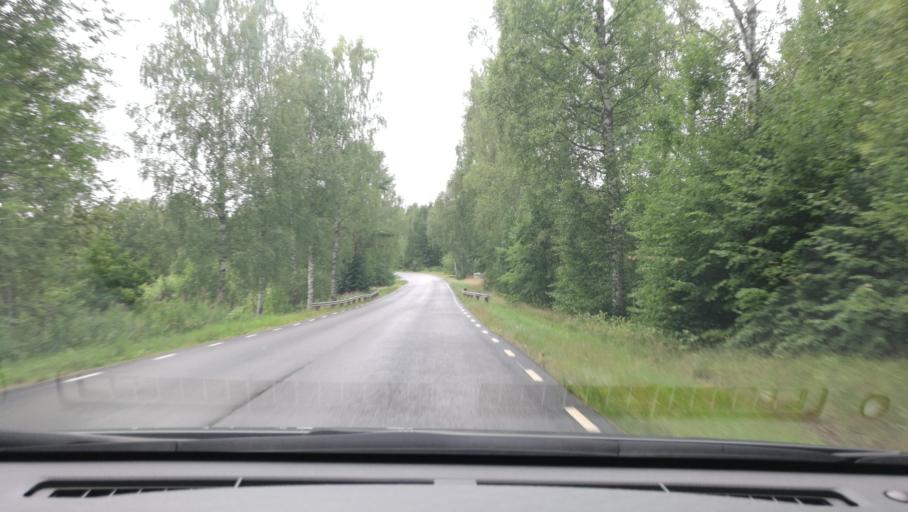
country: SE
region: OEstergoetland
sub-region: Norrkopings Kommun
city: Svartinge
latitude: 58.8242
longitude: 15.9708
